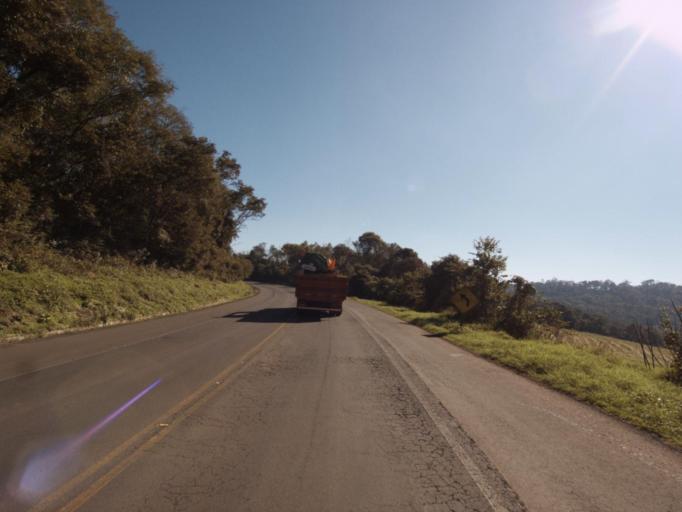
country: BR
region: Rio Grande do Sul
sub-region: Frederico Westphalen
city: Frederico Westphalen
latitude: -27.0621
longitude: -53.2210
